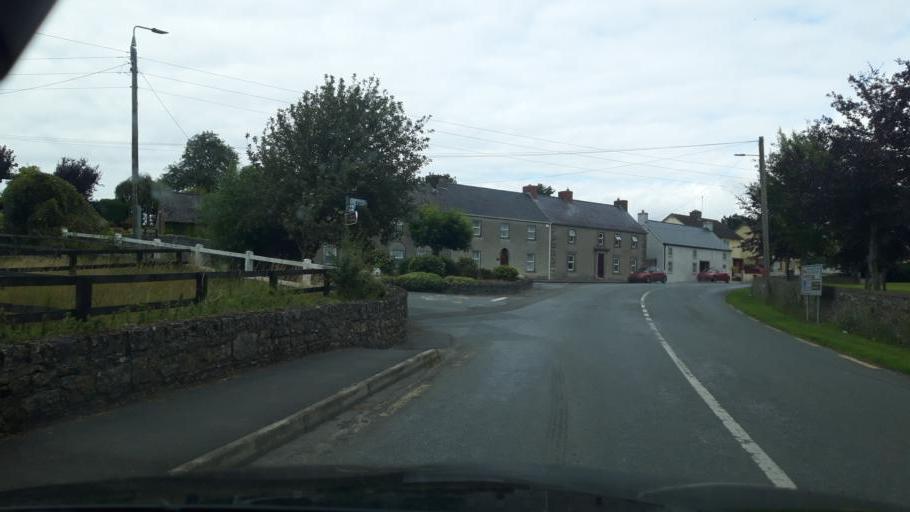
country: IE
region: Leinster
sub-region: Kilkenny
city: Thomastown
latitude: 52.6273
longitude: -7.0722
